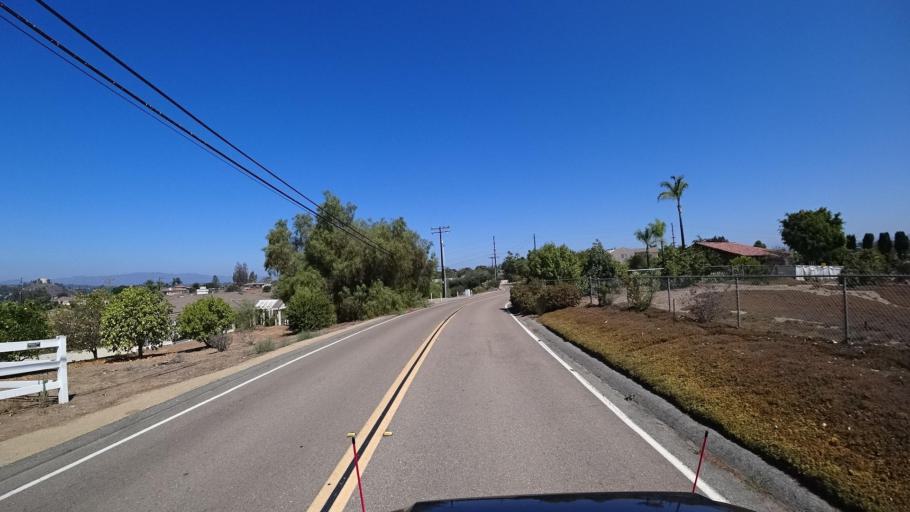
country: US
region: California
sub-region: San Diego County
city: Bonsall
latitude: 33.3281
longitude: -117.2222
